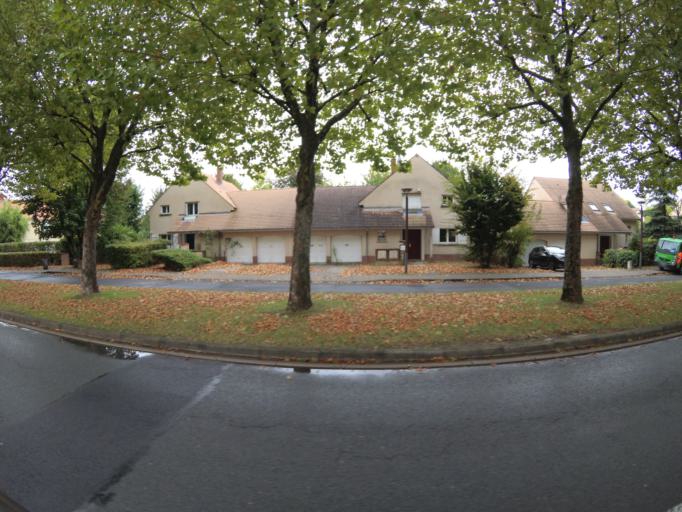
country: FR
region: Ile-de-France
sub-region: Departement de Seine-et-Marne
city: Bussy-Saint-Georges
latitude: 48.8432
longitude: 2.7052
